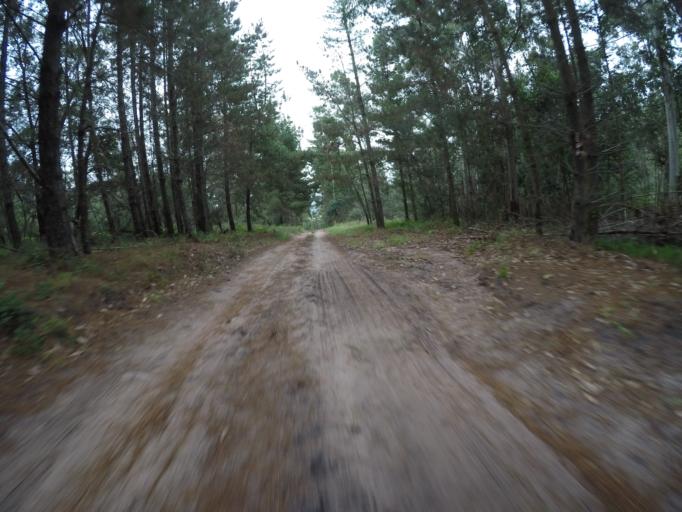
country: ZA
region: Western Cape
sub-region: Eden District Municipality
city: Knysna
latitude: -34.0096
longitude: 22.8080
